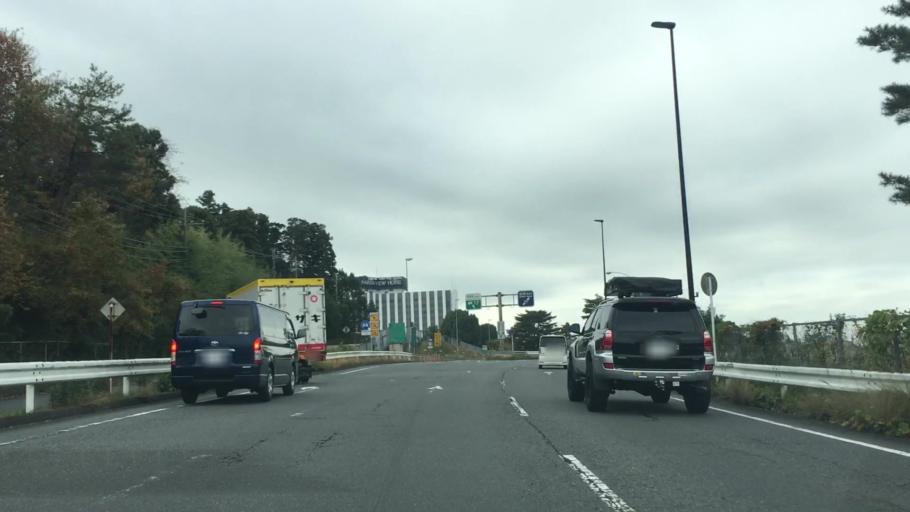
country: JP
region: Chiba
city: Narita
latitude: 35.7829
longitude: 140.3583
